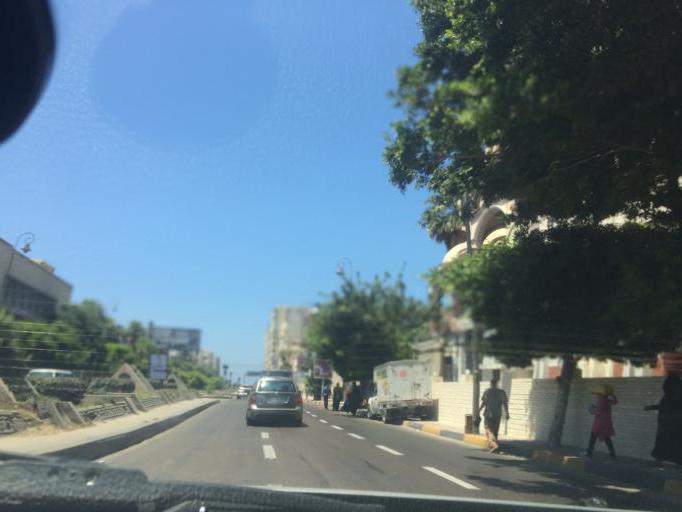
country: EG
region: Alexandria
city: Alexandria
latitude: 31.2061
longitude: 29.9141
